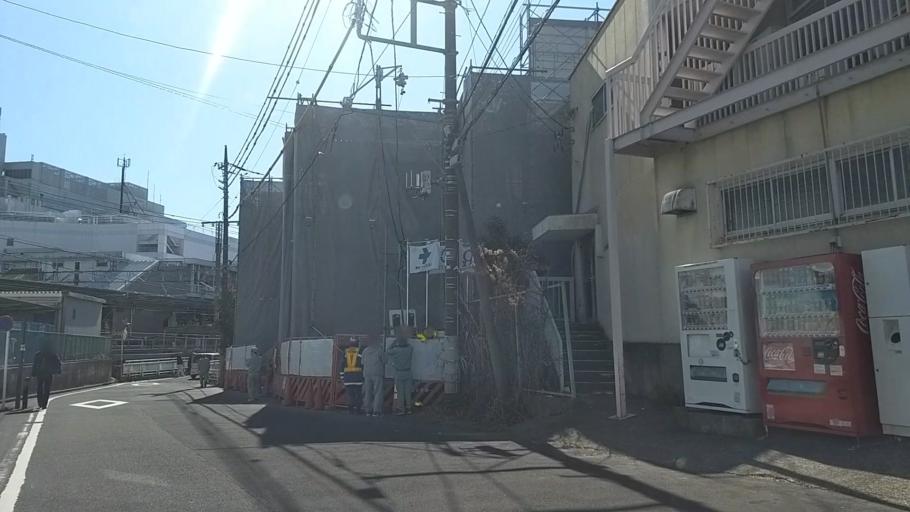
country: JP
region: Kanagawa
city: Kamakura
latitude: 35.3546
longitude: 139.5306
